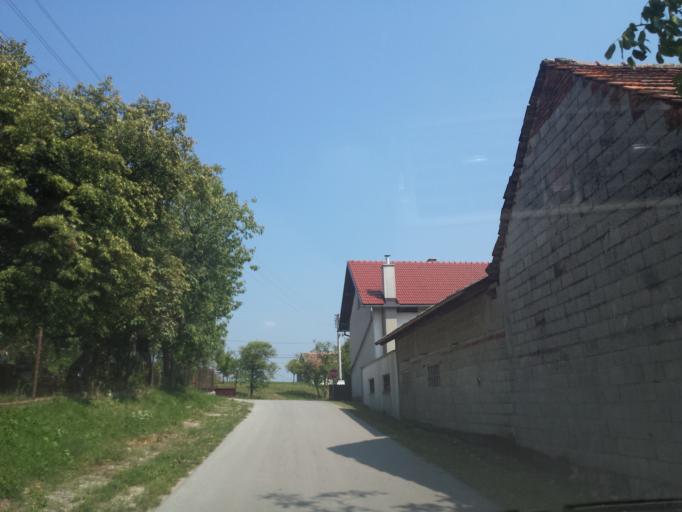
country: HR
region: Zagrebacka
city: Rude
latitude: 45.7228
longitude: 15.7080
